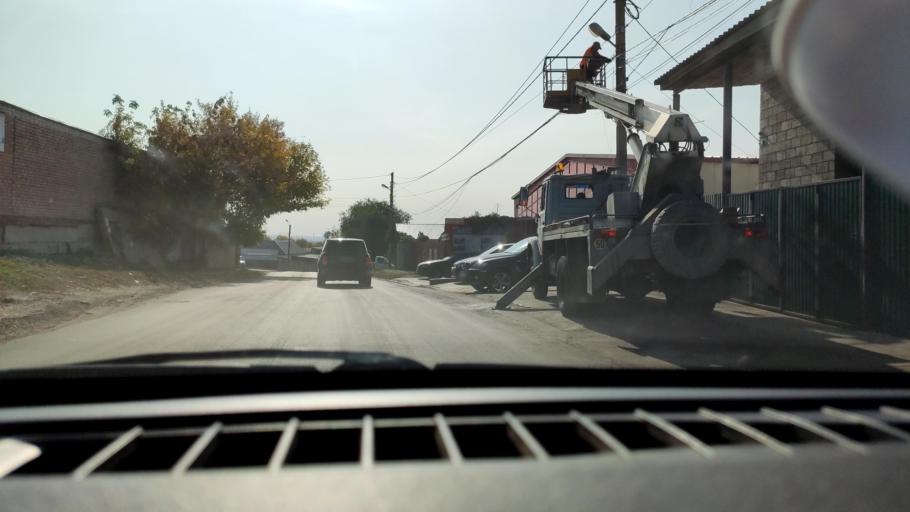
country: RU
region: Samara
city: Samara
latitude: 53.1792
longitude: 50.1566
